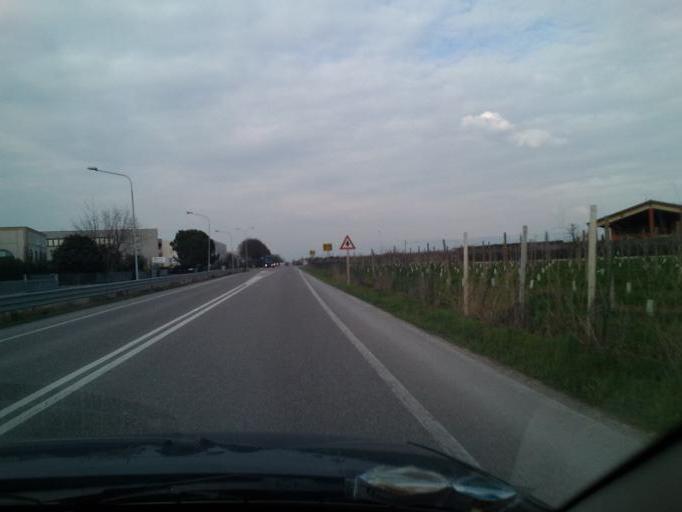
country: IT
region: Veneto
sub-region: Provincia di Verona
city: Sommacampagna
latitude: 45.4000
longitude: 10.8504
